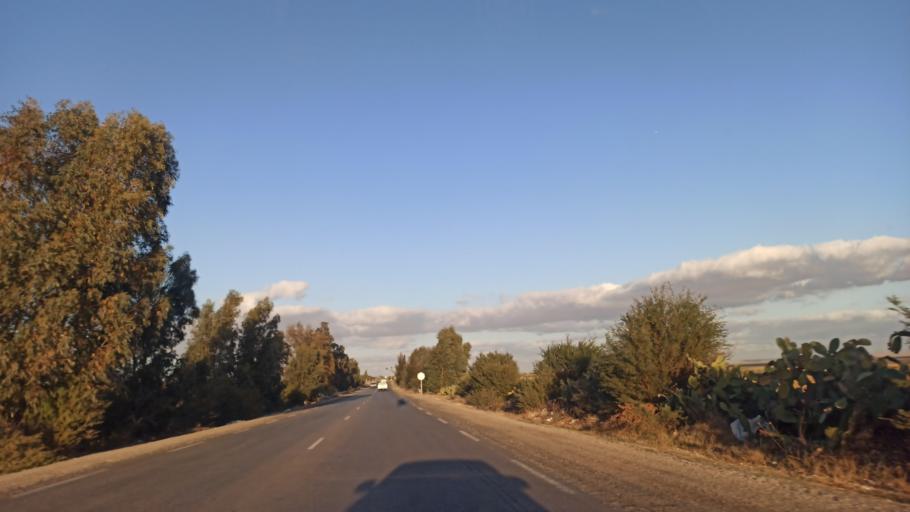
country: TN
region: Al Qayrawan
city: Sbikha
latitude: 35.8526
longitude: 10.1969
